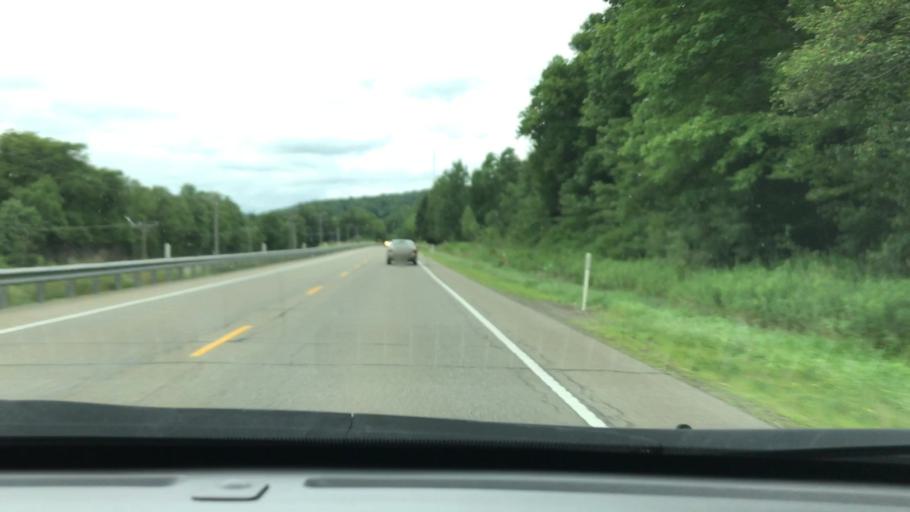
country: US
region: Pennsylvania
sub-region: Elk County
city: Johnsonburg
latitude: 41.5498
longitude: -78.6826
